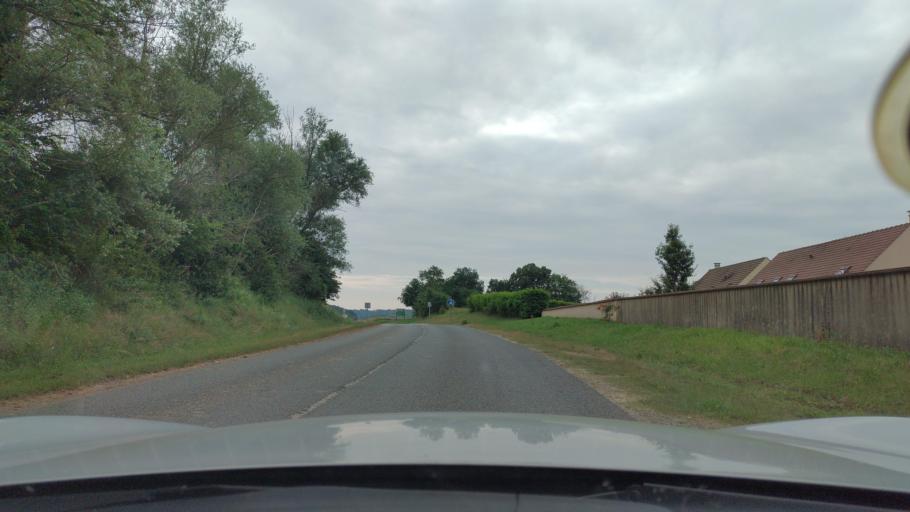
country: FR
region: Picardie
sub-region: Departement de l'Oise
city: Betz
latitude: 49.1007
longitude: 2.9606
